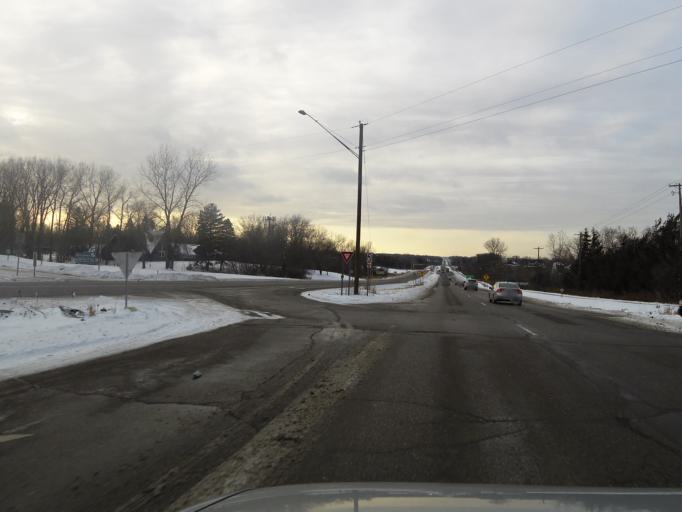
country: US
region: Minnesota
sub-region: Dakota County
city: West Saint Paul
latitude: 44.8835
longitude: -93.0994
